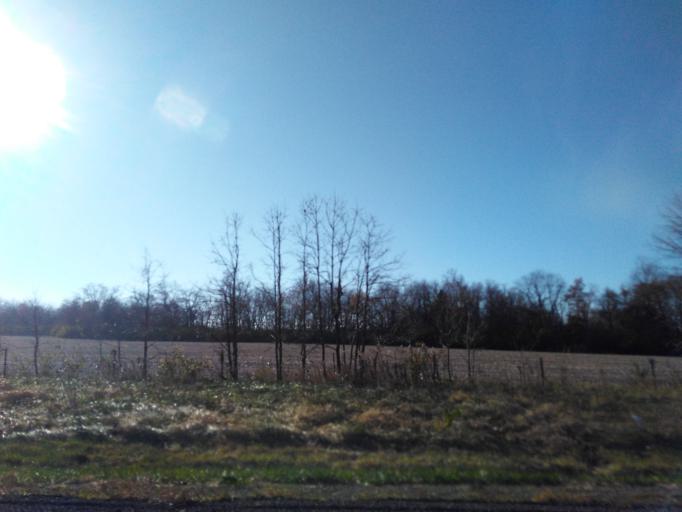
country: US
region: Illinois
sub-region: Madison County
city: Highland
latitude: 38.7864
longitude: -89.6766
